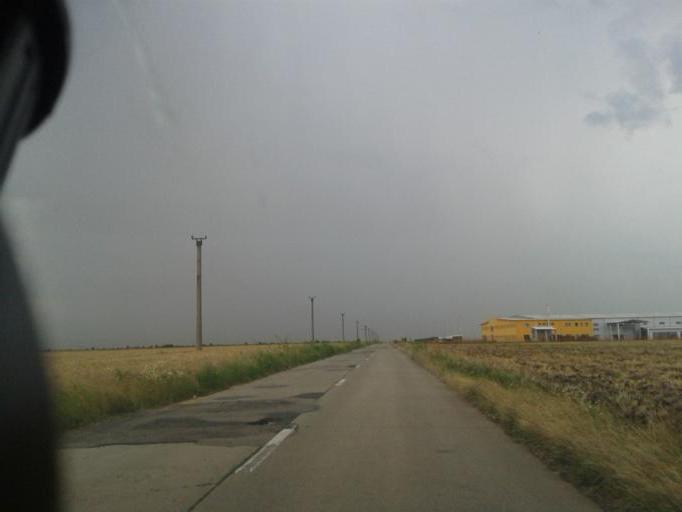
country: RO
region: Ialomita
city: Sinesti
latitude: 44.5418
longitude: 26.4041
